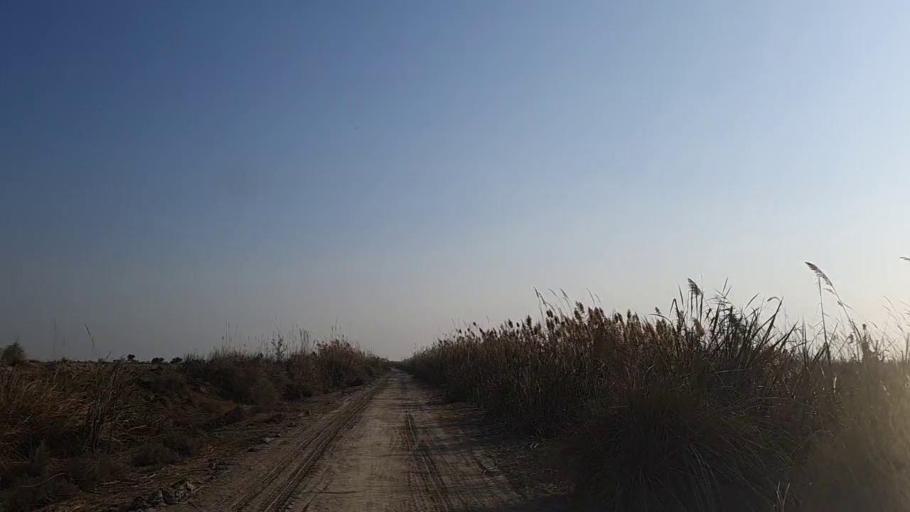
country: PK
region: Sindh
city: Daur
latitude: 26.4353
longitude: 68.3525
